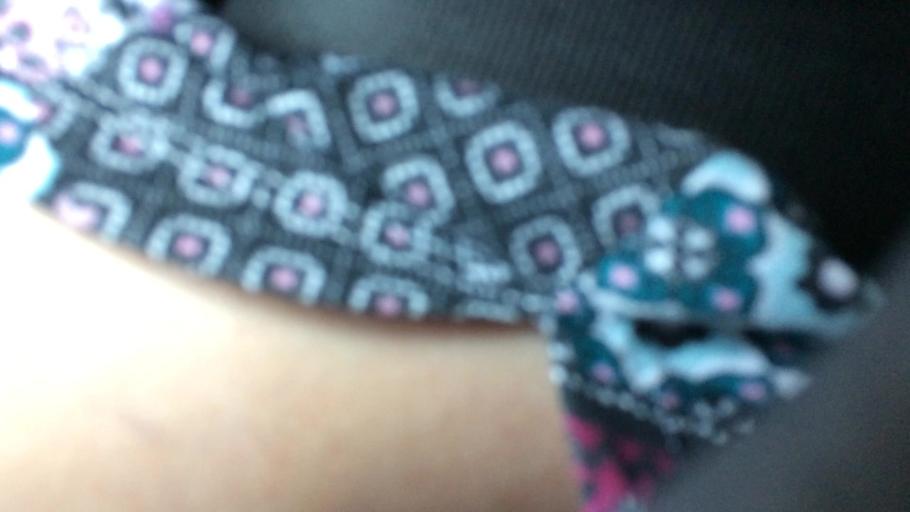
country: US
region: New Mexico
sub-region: Colfax County
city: Springer
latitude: 36.2313
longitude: -104.6543
